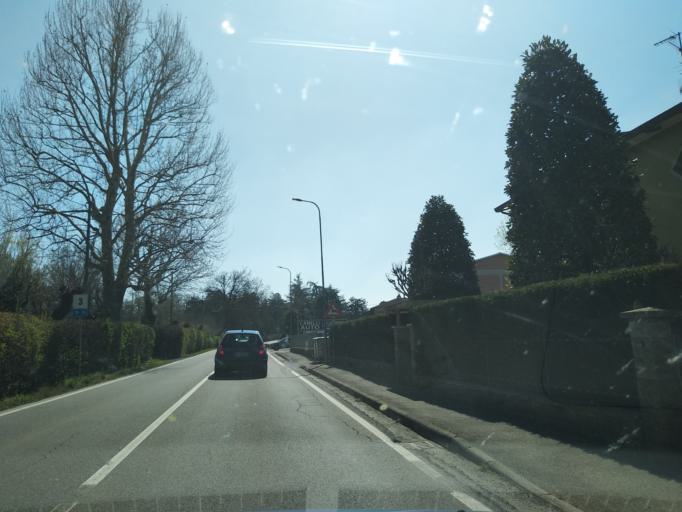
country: IT
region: Emilia-Romagna
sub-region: Provincia di Reggio Emilia
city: Albinea
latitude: 44.6312
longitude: 10.6056
